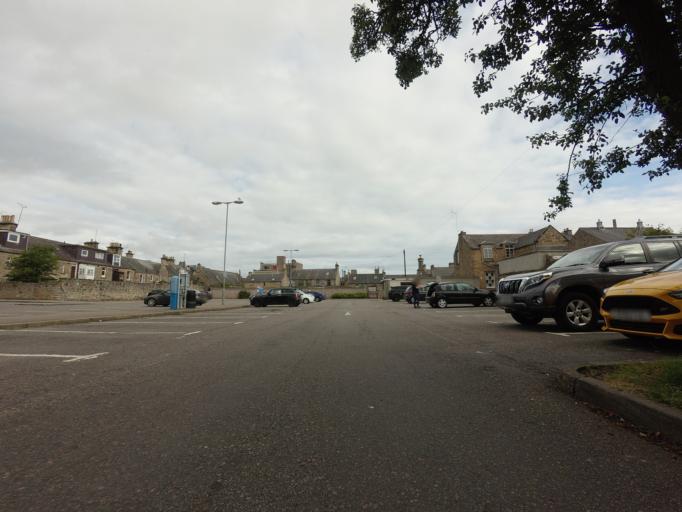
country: GB
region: Scotland
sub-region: Moray
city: Elgin
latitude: 57.6469
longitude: -3.3140
